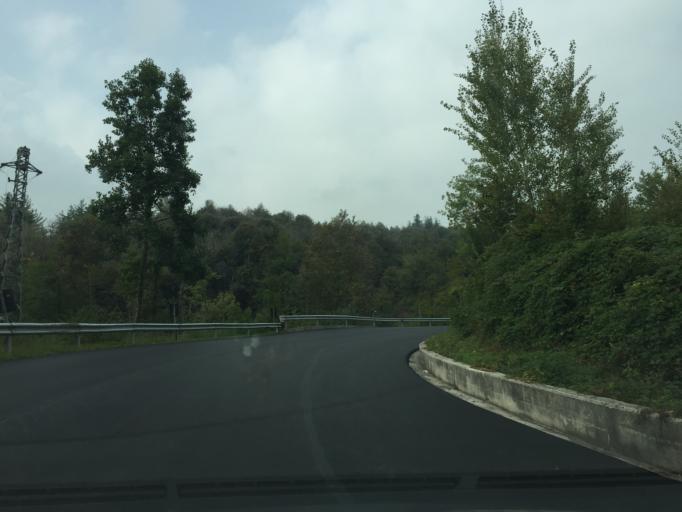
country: IT
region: Piedmont
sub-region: Provincia di Cuneo
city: Roccaforte Mondovi
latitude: 44.3089
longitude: 7.7112
